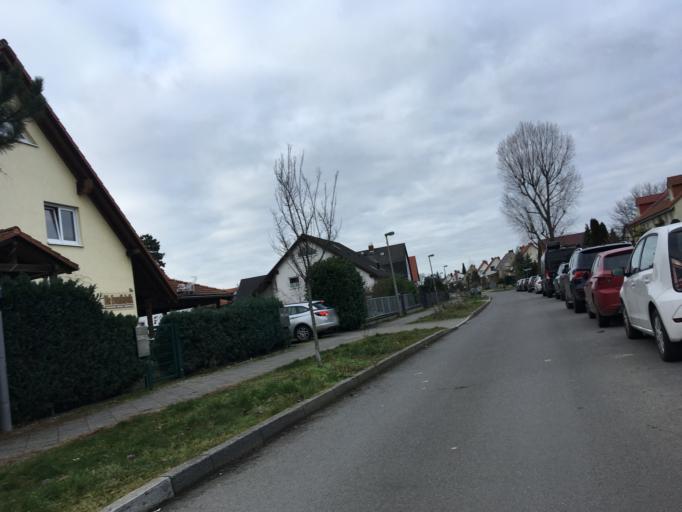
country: DE
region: Berlin
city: Buchholz
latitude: 52.5909
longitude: 13.4272
